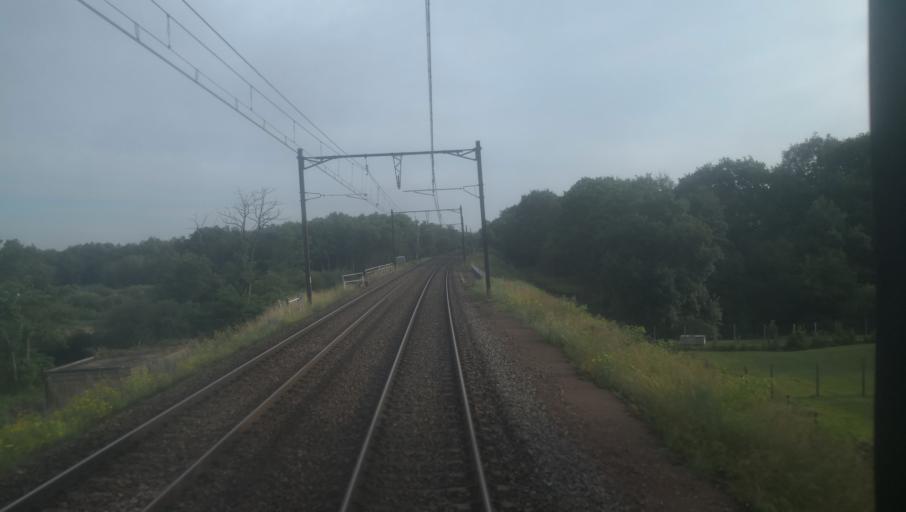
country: FR
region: Centre
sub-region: Departement du Loiret
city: La Ferte-Saint-Aubin
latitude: 47.7255
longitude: 1.9306
